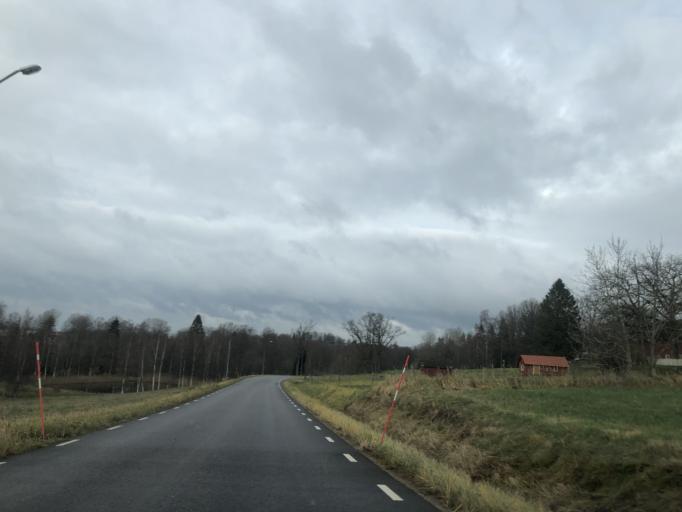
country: SE
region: Vaestra Goetaland
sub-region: Ulricehamns Kommun
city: Ulricehamn
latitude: 57.8175
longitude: 13.2447
